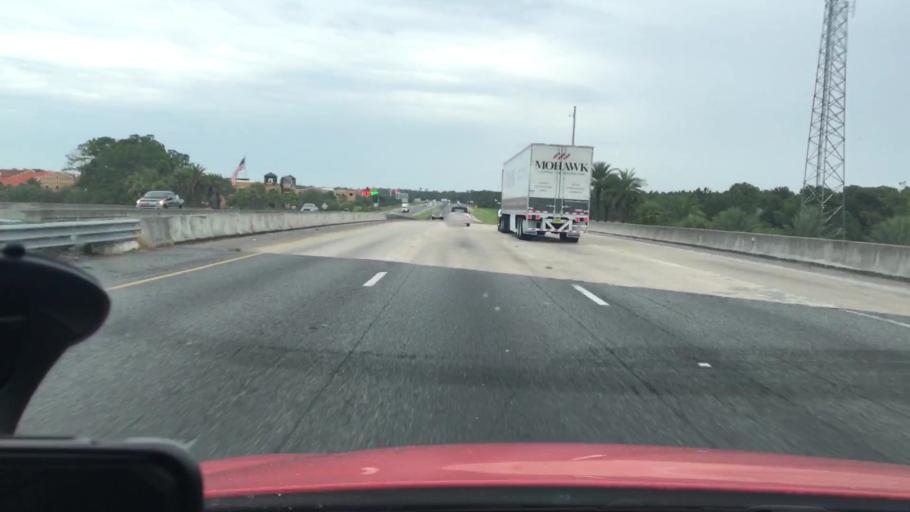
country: US
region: Florida
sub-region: Volusia County
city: Ormond-by-the-Sea
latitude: 29.3342
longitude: -81.1347
